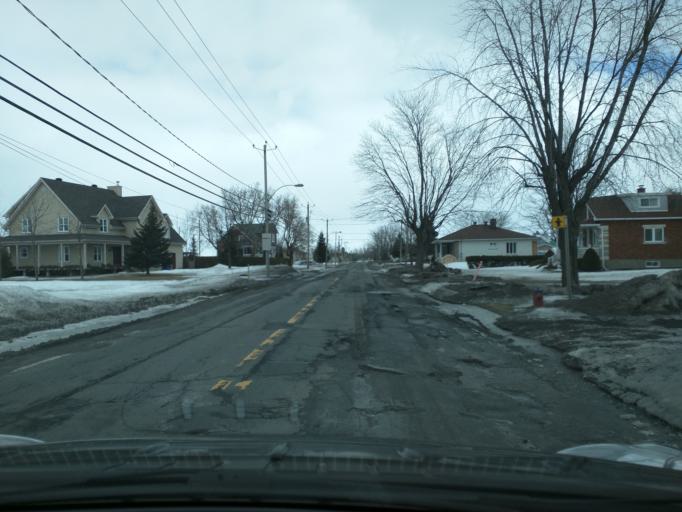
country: CA
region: Quebec
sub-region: Monteregie
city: Sainte-Julie
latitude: 45.6569
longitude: -73.2911
